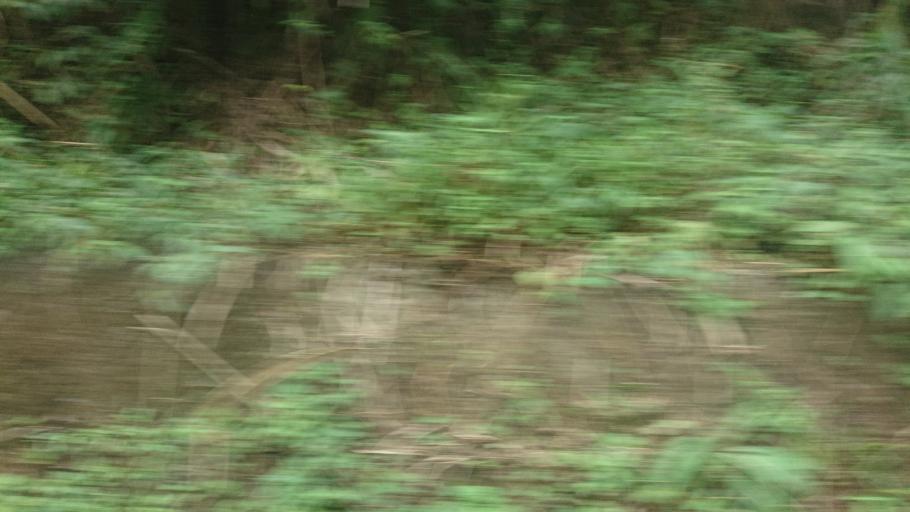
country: TW
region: Taiwan
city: Lugu
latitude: 23.6278
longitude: 120.7093
